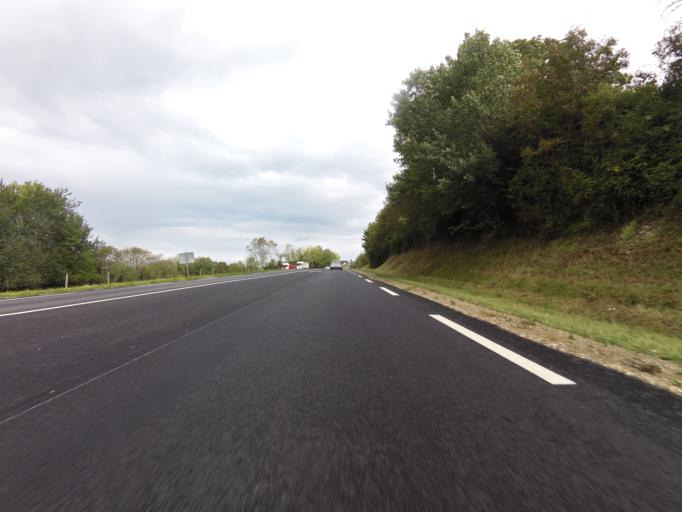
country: FR
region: Haute-Normandie
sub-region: Departement de la Seine-Maritime
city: Criel-sur-Mer
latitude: 50.0154
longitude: 1.3230
